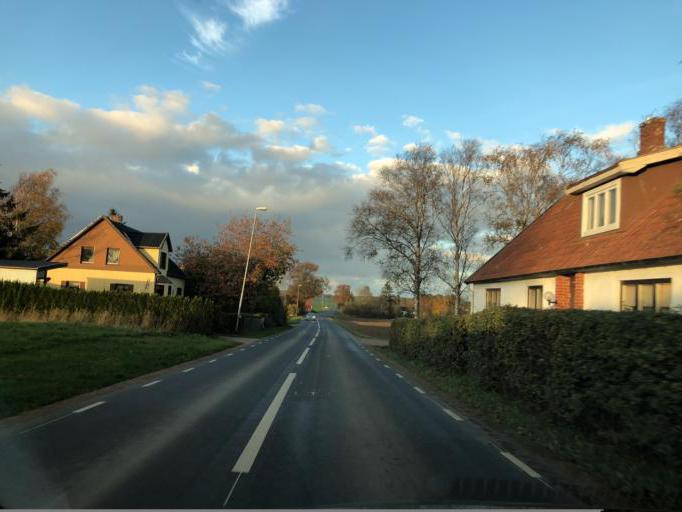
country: SE
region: Skane
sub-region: Svalovs Kommun
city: Svaloev
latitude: 55.8989
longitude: 13.1888
